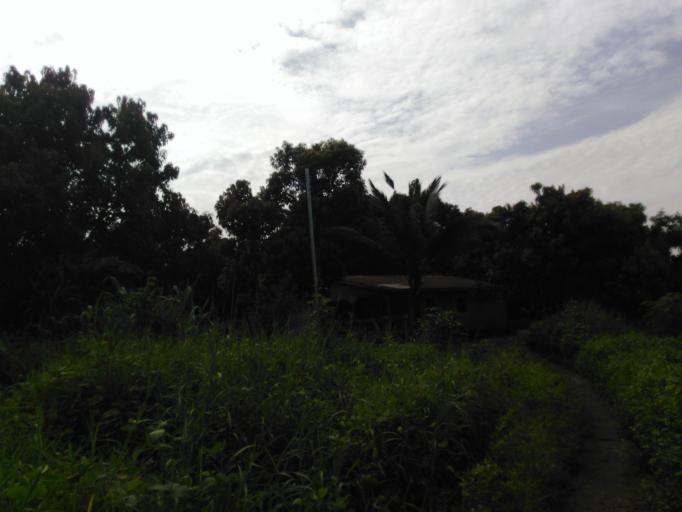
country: SL
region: Southern Province
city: Rotifunk
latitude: 8.4837
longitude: -12.7573
